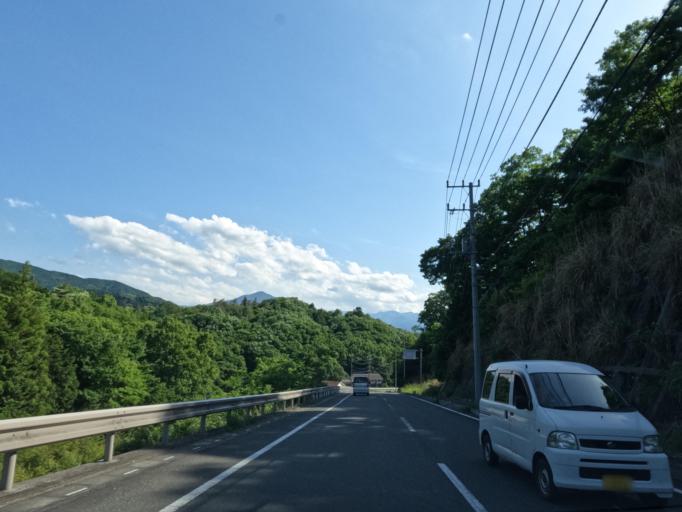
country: JP
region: Saitama
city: Chichibu
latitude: 36.0310
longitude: 139.1260
